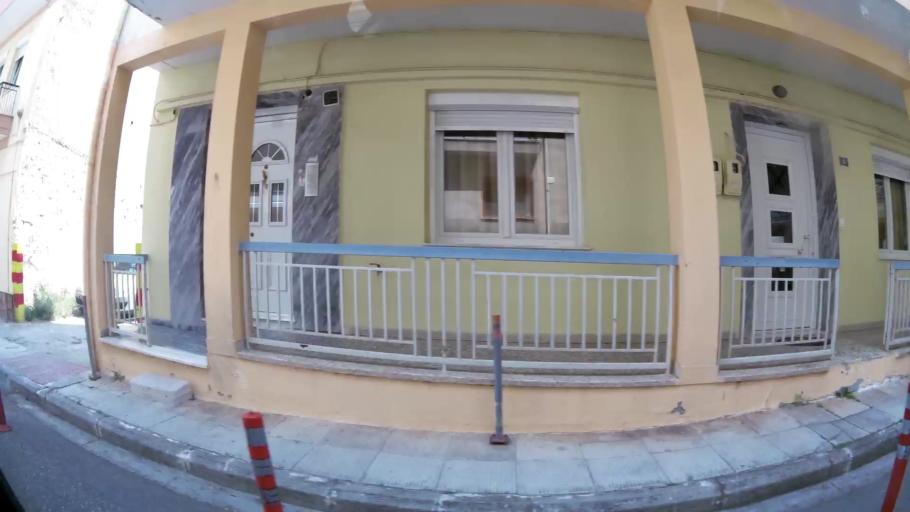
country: GR
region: West Macedonia
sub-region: Nomos Kozanis
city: Kozani
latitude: 40.2977
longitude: 21.7879
